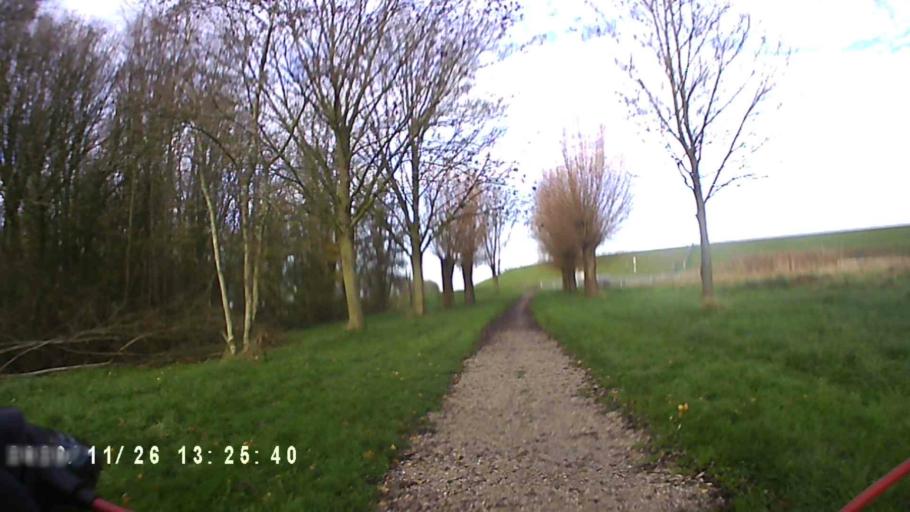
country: NL
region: Groningen
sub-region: Gemeente Delfzijl
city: Delfzijl
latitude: 53.3459
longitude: 6.9025
